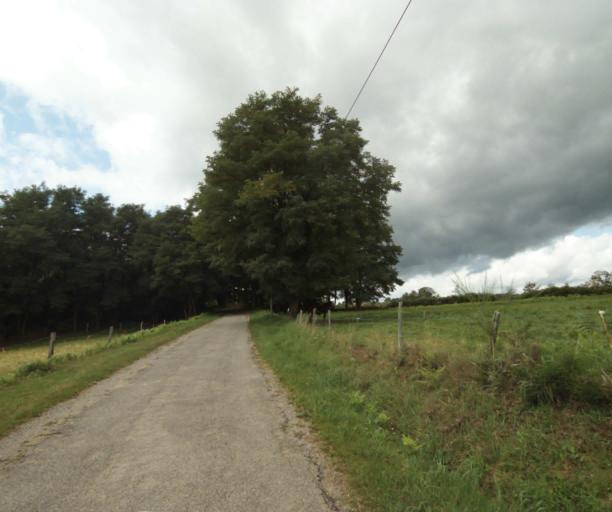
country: FR
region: Limousin
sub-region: Departement de la Correze
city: Sainte-Fortunade
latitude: 45.1668
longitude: 1.8149
